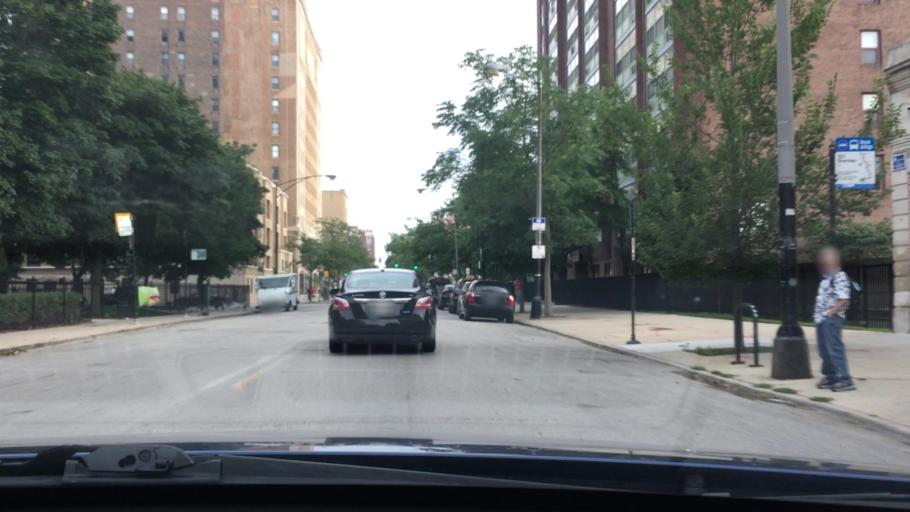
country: US
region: Illinois
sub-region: Cook County
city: Evanston
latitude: 41.9671
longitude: -87.6548
